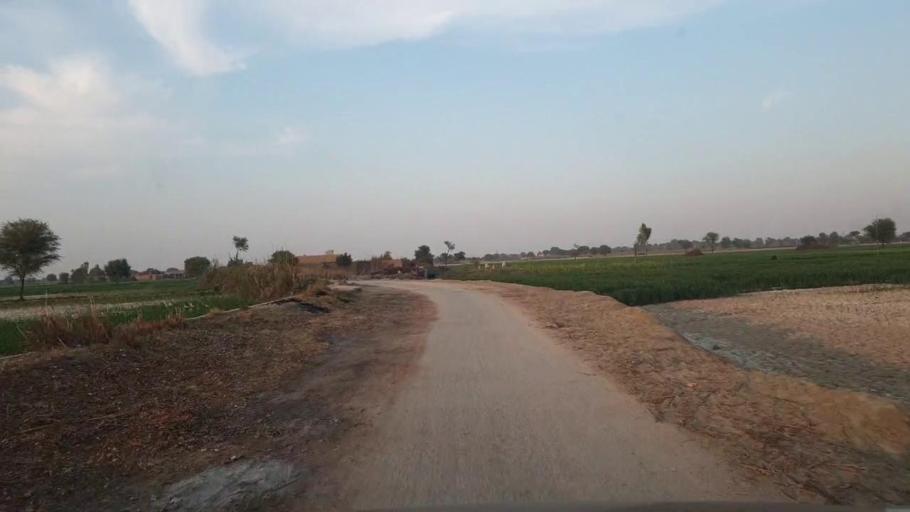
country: PK
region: Sindh
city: Shahpur Chakar
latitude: 26.1911
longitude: 68.6172
